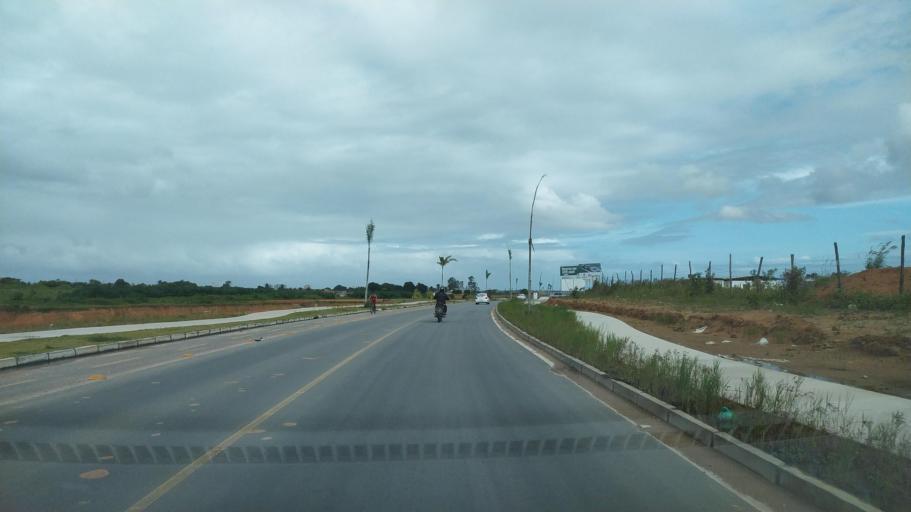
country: BR
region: Alagoas
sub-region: Satuba
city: Satuba
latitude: -9.5346
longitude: -35.7668
